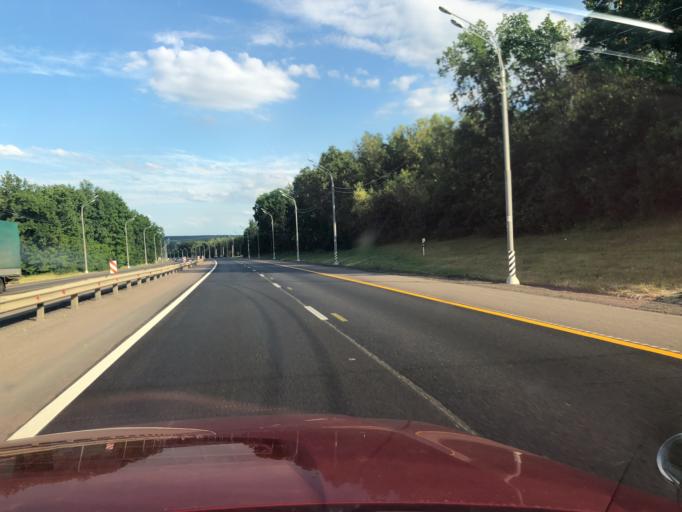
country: RU
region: Lipetsk
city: Zadonsk
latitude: 52.3852
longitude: 38.8695
